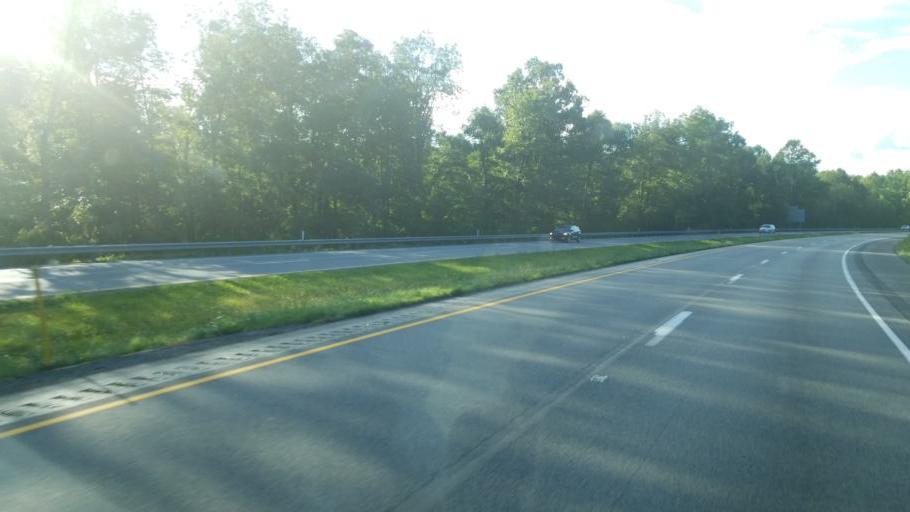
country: US
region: Maryland
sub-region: Washington County
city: Hancock
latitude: 39.7919
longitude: -78.2128
